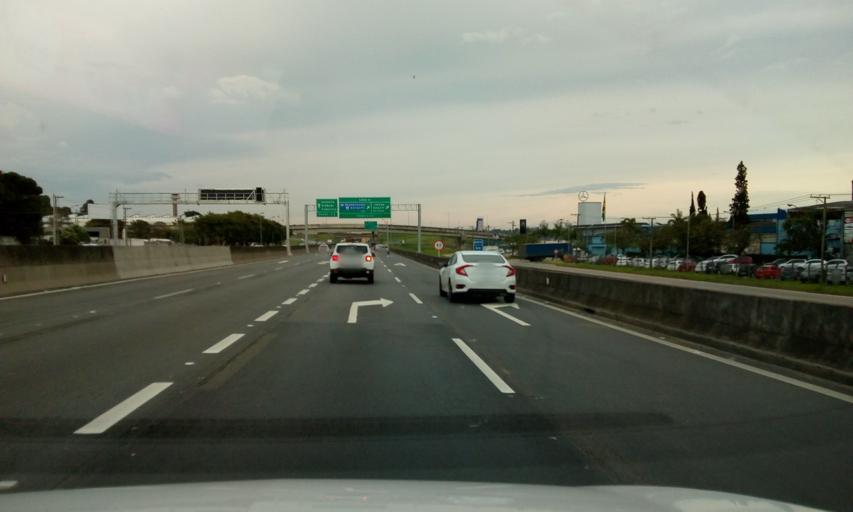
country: BR
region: Sao Paulo
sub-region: Jundiai
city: Jundiai
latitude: -23.1758
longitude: -46.9179
